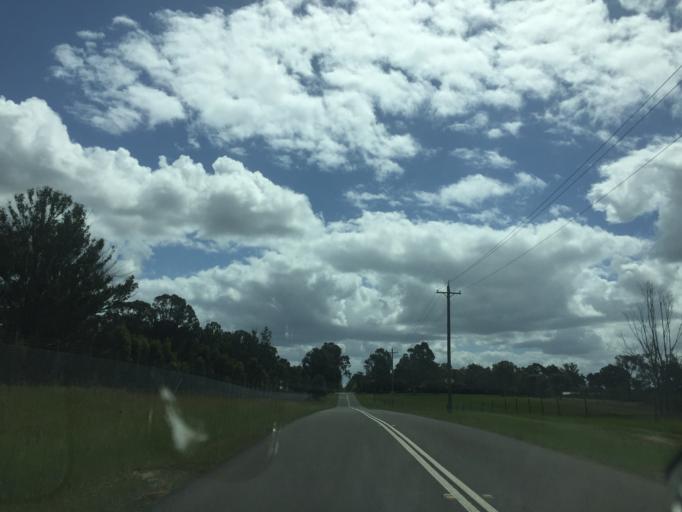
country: AU
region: New South Wales
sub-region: Penrith Municipality
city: Kingswood Park
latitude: -33.7989
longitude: 150.7364
